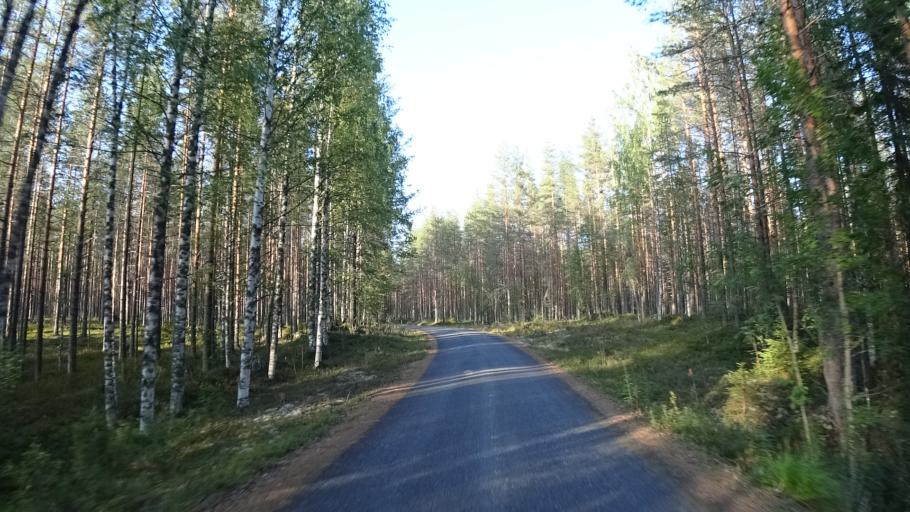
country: FI
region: North Karelia
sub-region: Joensuu
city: Ilomantsi
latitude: 63.1300
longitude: 30.7167
